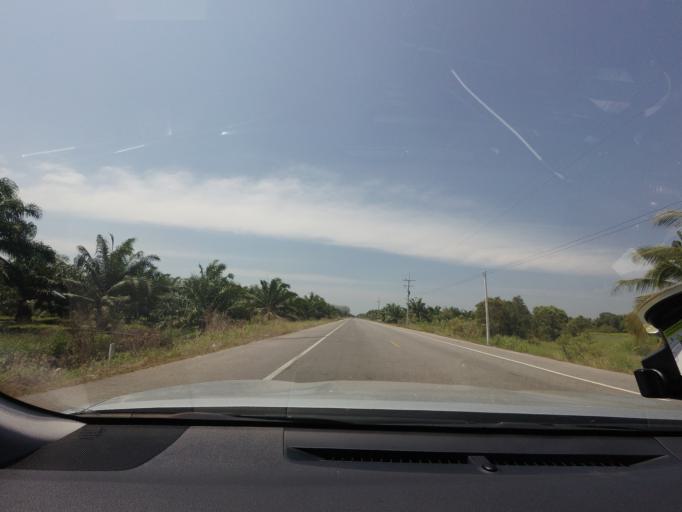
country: TH
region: Surat Thani
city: Tha Chang
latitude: 9.2177
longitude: 99.2097
